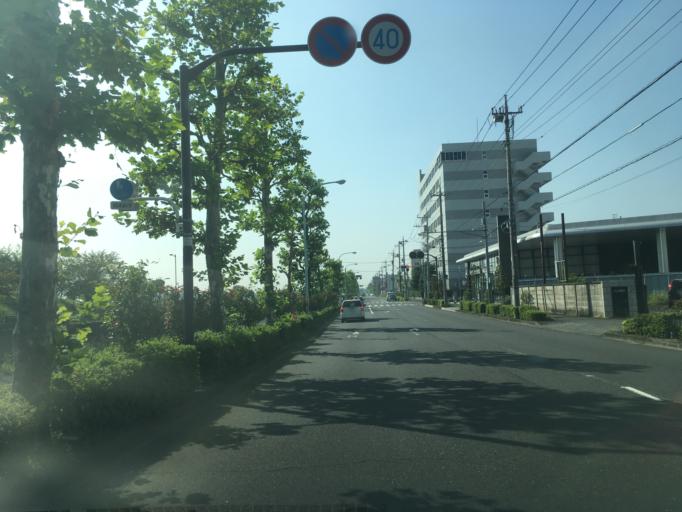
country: JP
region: Tokyo
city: Fussa
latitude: 35.7430
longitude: 139.3829
